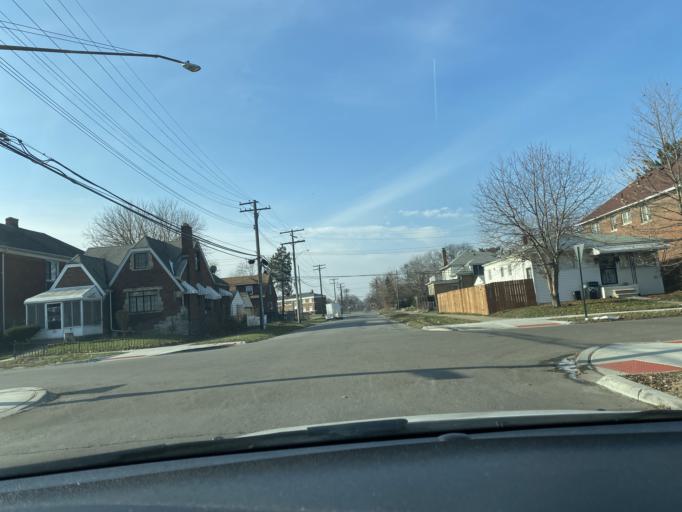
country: US
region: Michigan
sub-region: Wayne County
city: Highland Park
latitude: 42.3792
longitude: -83.1423
